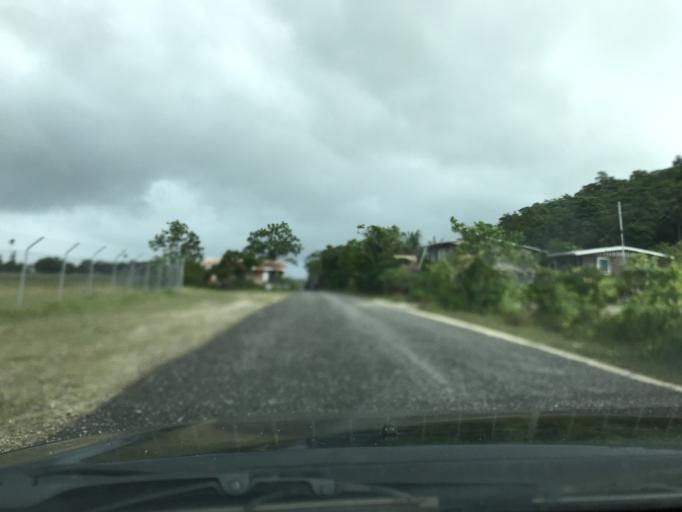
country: SB
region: Western Province
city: Gizo
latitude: -8.3253
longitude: 157.2671
